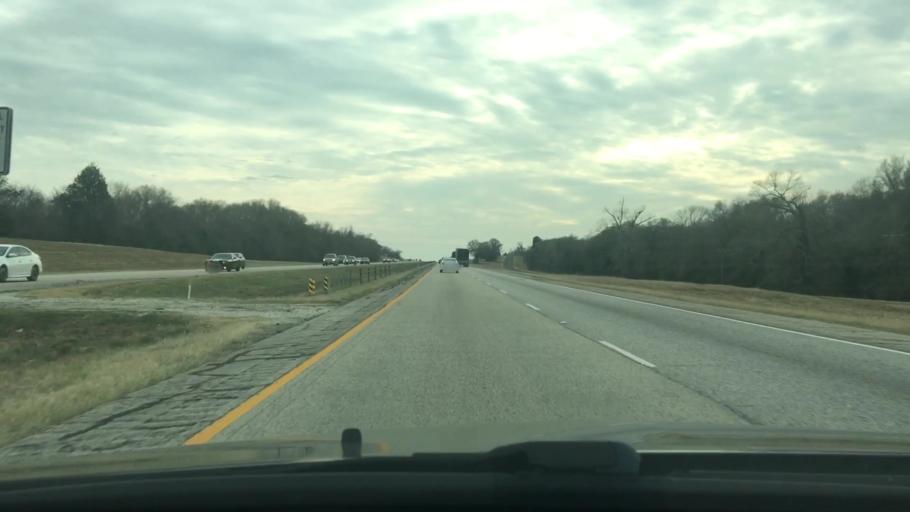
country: US
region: Texas
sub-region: Leon County
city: Centerville
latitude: 31.2310
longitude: -95.9945
